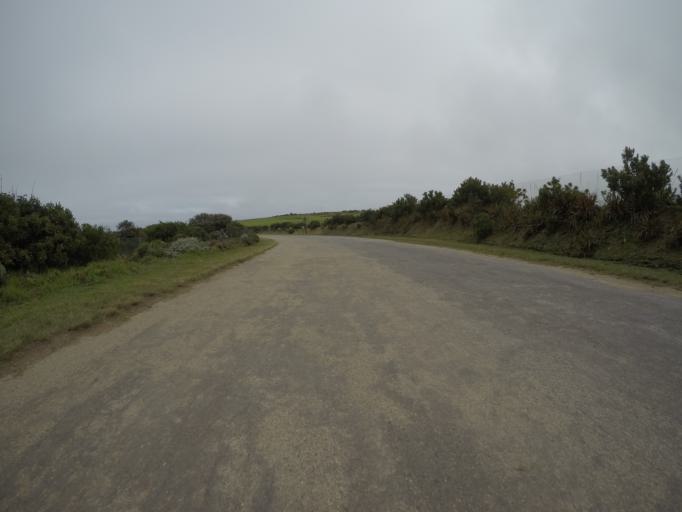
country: ZA
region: Eastern Cape
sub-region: Cacadu District Municipality
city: Kareedouw
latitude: -34.0711
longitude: 24.2335
